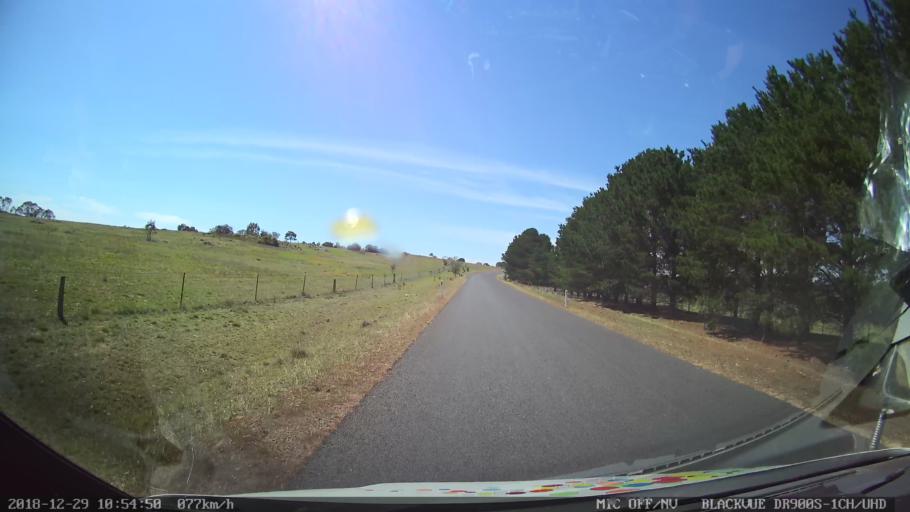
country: AU
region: New South Wales
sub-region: Palerang
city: Bungendore
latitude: -35.1183
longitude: 149.5297
